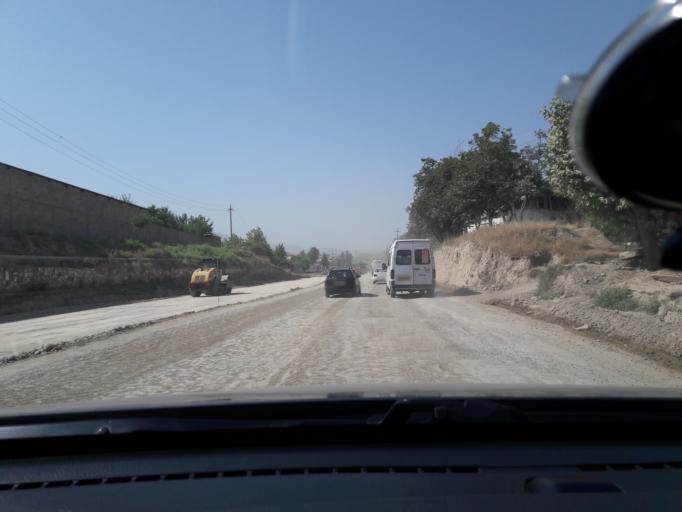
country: TJ
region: Dushanbe
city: Boshkengash
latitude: 38.4456
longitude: 68.7332
